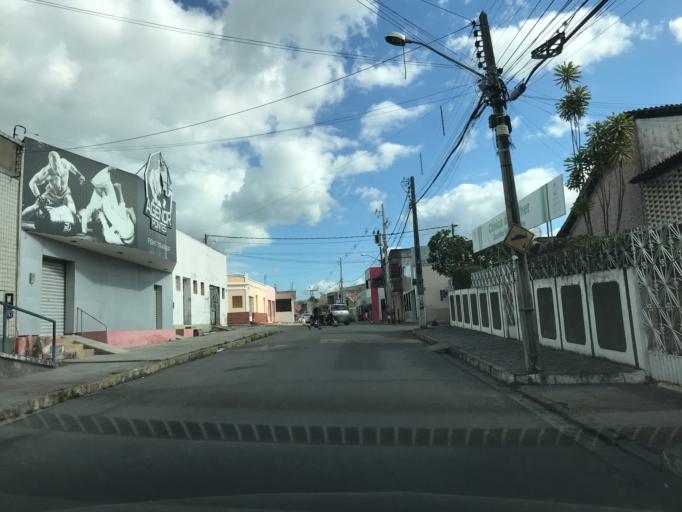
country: BR
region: Pernambuco
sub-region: Bezerros
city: Bezerros
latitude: -8.2385
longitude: -35.7536
